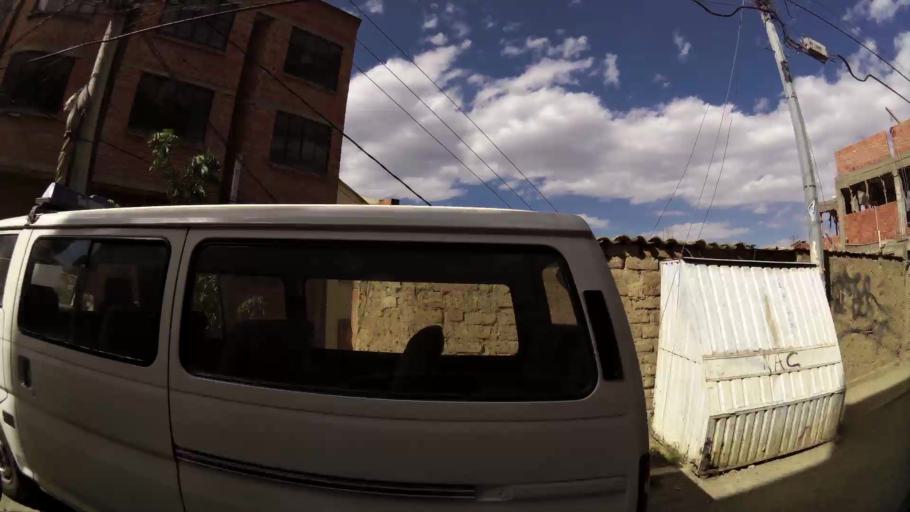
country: BO
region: La Paz
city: La Paz
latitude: -16.4761
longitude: -68.1260
